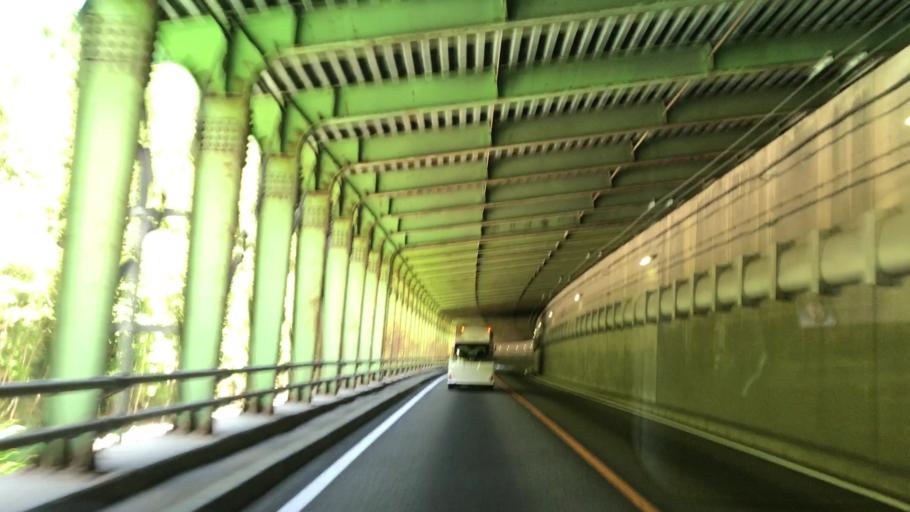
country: JP
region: Hokkaido
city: Shimo-furano
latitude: 42.9400
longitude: 142.6021
